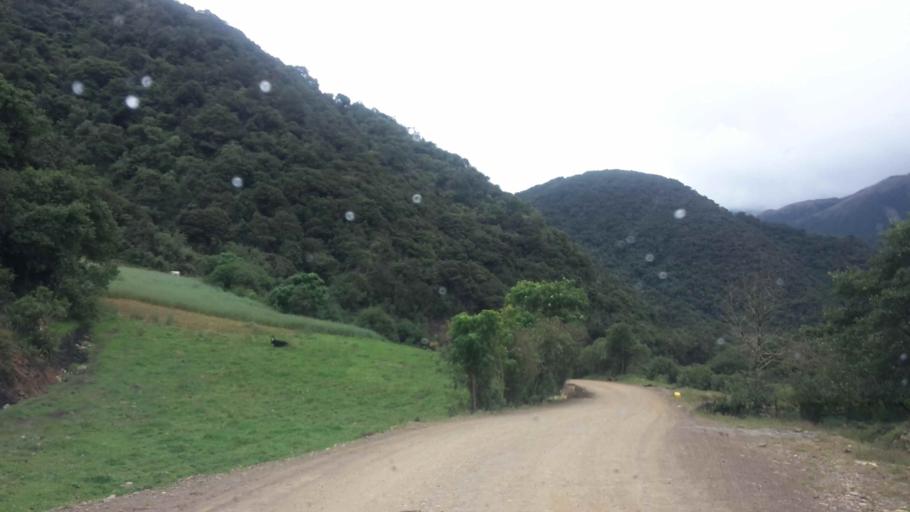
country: BO
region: Cochabamba
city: Totora
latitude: -17.5655
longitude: -65.2773
